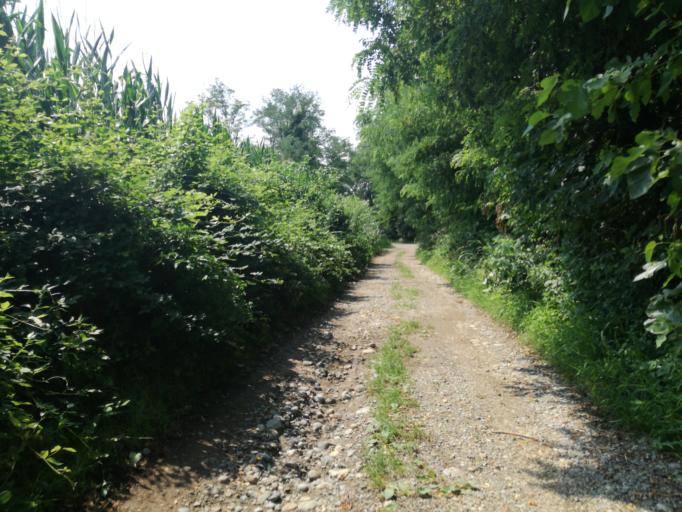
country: IT
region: Lombardy
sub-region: Provincia di Bergamo
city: Calusco d'Adda
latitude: 45.6767
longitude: 9.4742
